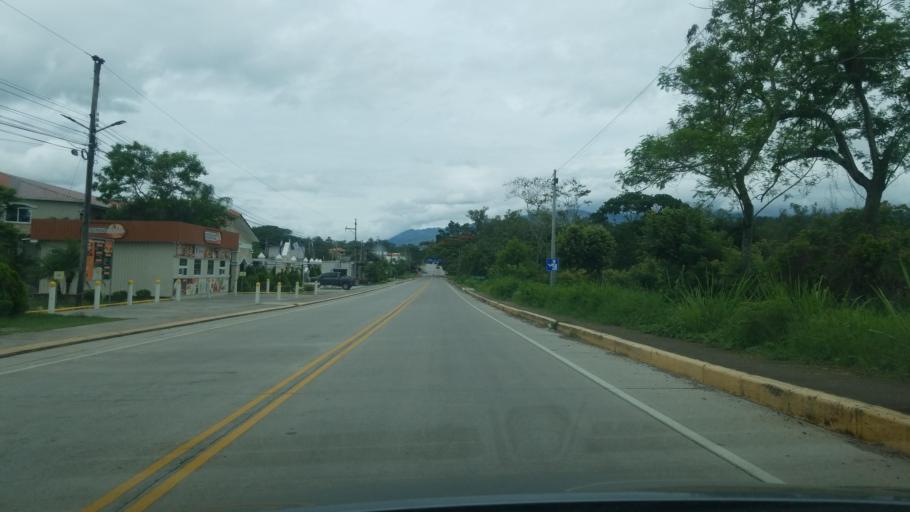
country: HN
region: Copan
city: La Entrada
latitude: 15.0701
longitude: -88.7660
